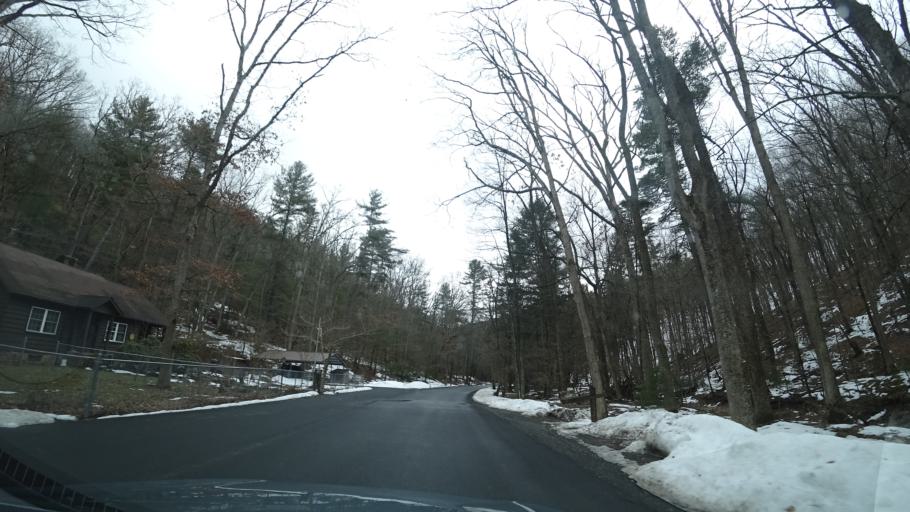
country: US
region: Virginia
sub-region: Shenandoah County
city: Basye
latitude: 38.9008
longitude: -78.9174
